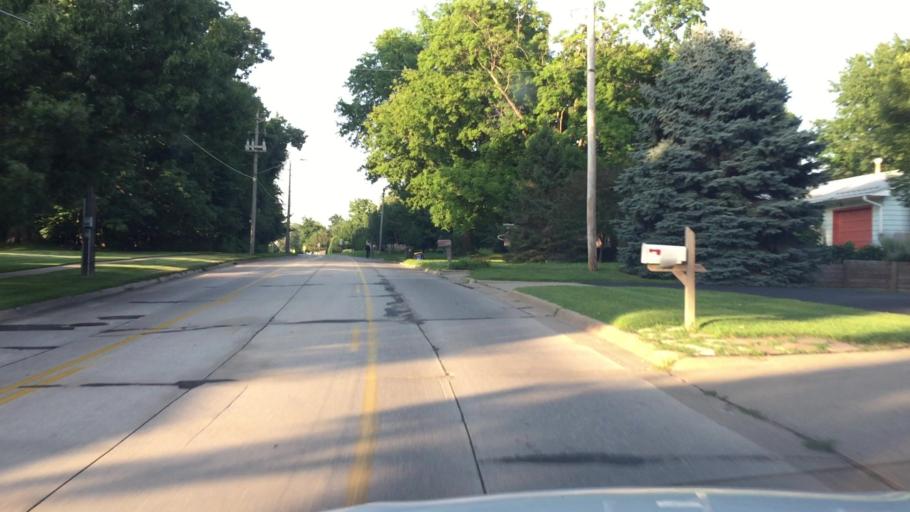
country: US
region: Iowa
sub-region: Johnson County
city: Iowa City
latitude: 41.6640
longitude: -91.5067
